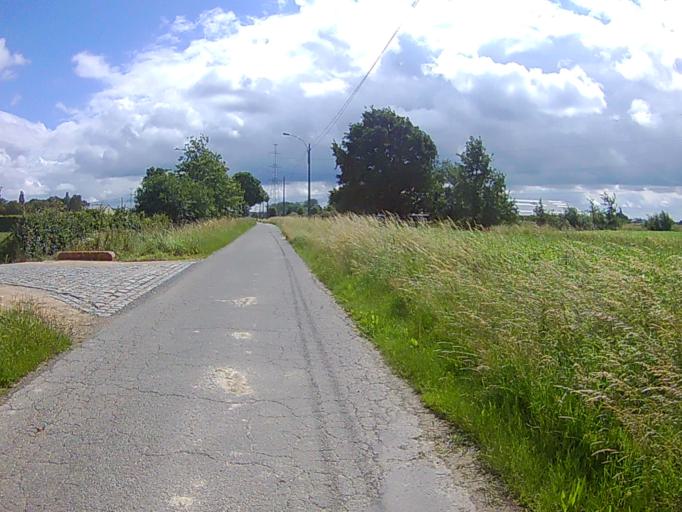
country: BE
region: Flanders
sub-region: Provincie Antwerpen
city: Ranst
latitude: 51.1630
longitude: 4.5451
